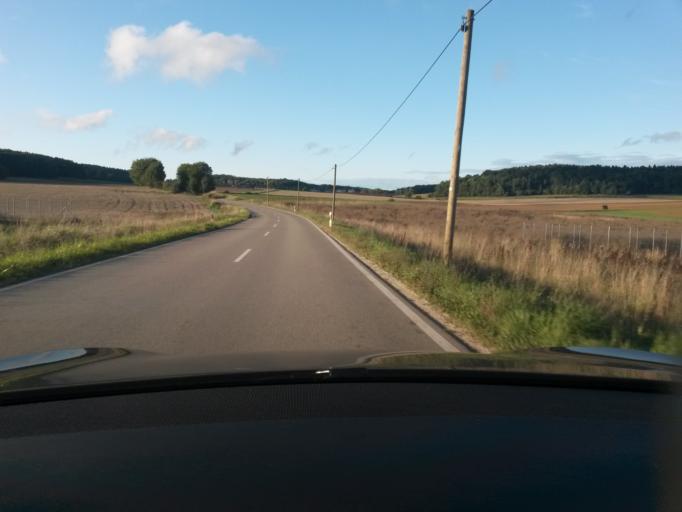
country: DE
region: Bavaria
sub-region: Upper Palatinate
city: Hohenfels
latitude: 49.1700
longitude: 11.8234
